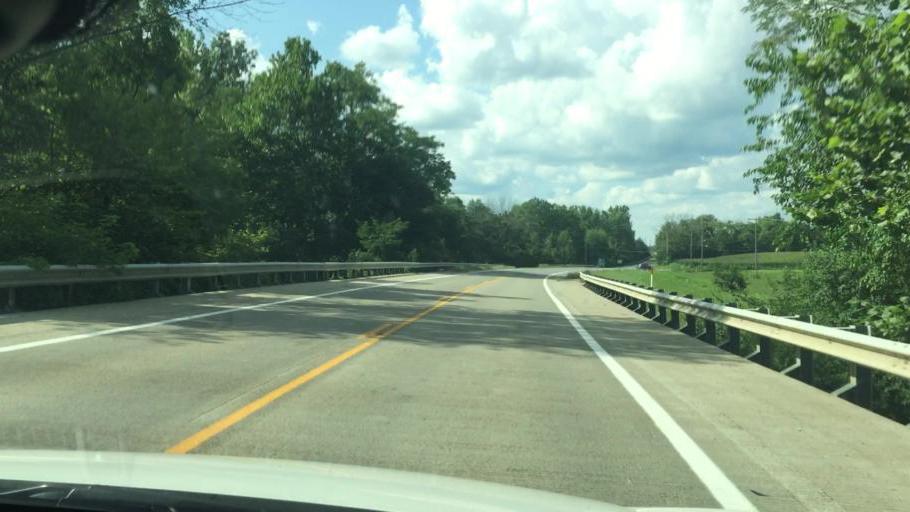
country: US
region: Ohio
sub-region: Madison County
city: Choctaw Lake
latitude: 39.9454
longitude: -83.5020
